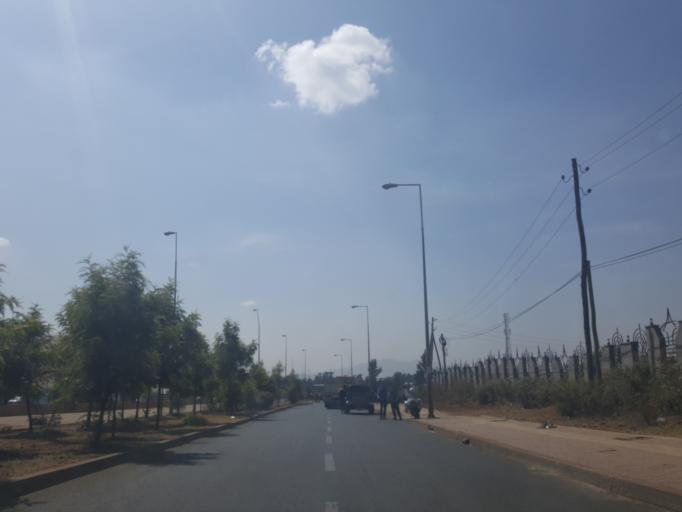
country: ET
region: Adis Abeba
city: Addis Ababa
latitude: 9.0641
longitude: 38.7146
